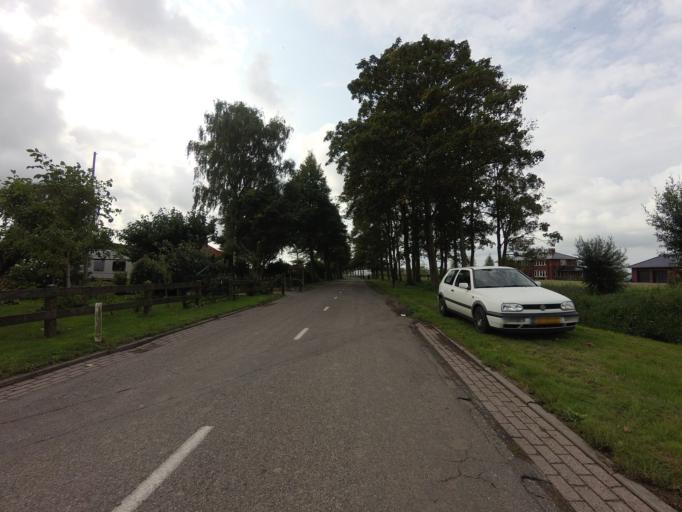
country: NL
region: North Holland
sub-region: Gemeente Medemblik
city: Opperdoes
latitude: 52.7038
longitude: 5.0559
